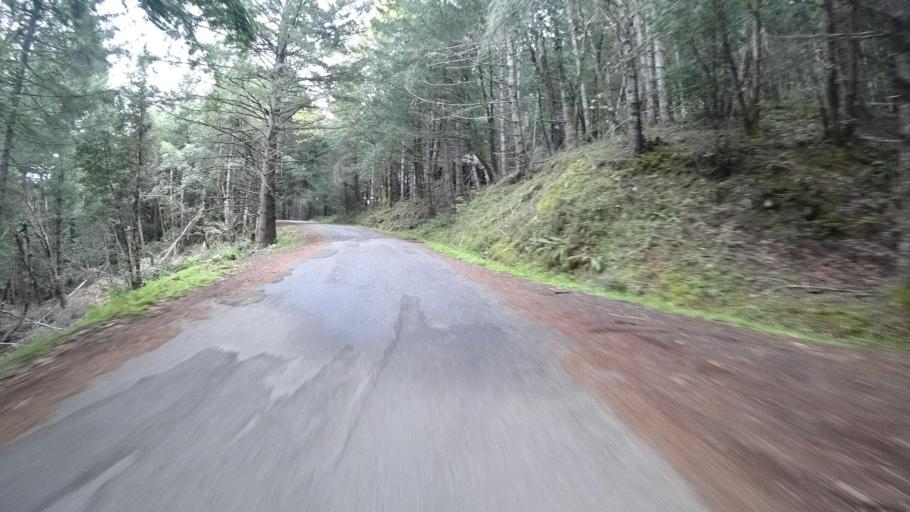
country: US
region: California
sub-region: Humboldt County
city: Redway
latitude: 40.2140
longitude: -123.7464
